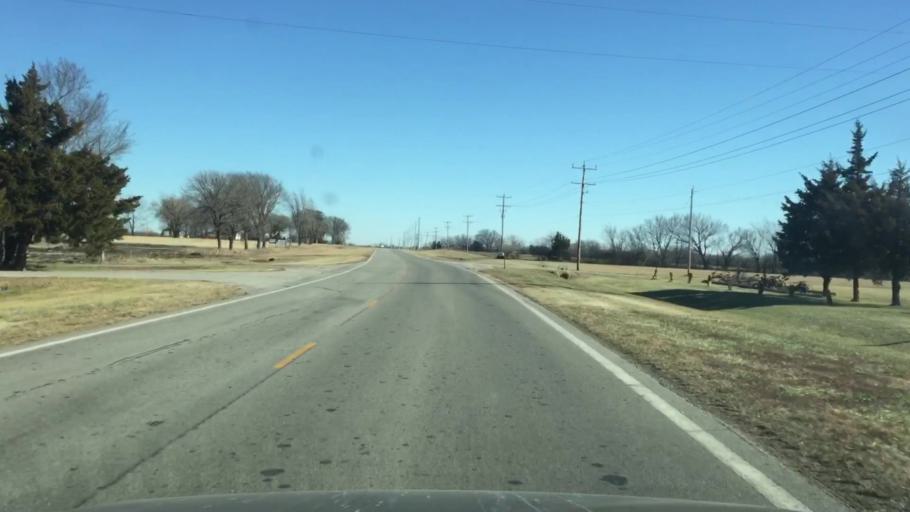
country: US
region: Kansas
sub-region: Allen County
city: Humboldt
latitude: 37.8201
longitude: -95.4267
